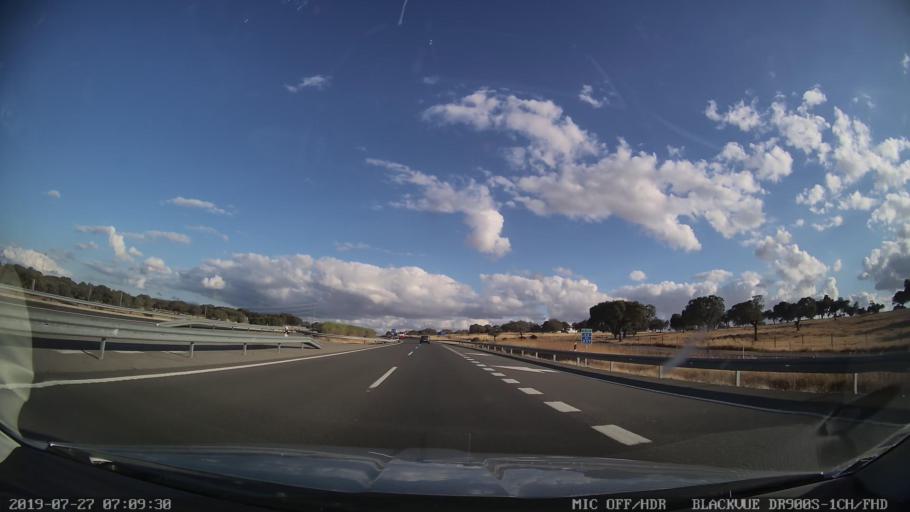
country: ES
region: Extremadura
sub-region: Provincia de Caceres
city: Jaraicejo
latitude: 39.5928
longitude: -5.8376
